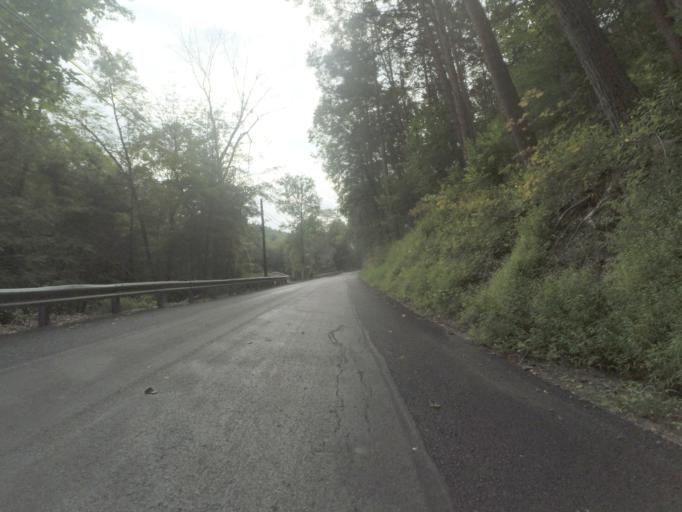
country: US
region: Pennsylvania
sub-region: Centre County
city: Zion
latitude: 41.0506
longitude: -77.6917
